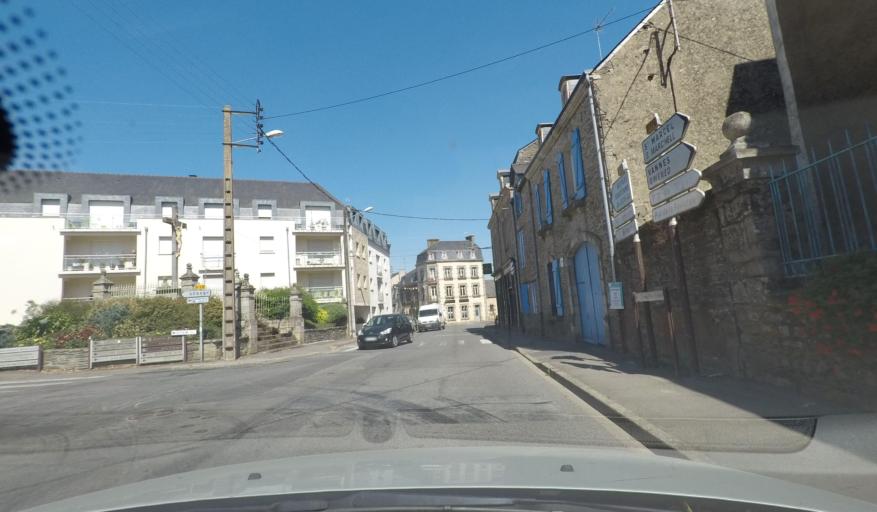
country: FR
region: Brittany
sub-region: Departement du Morbihan
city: Malestroit
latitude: 47.8088
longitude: -2.3842
